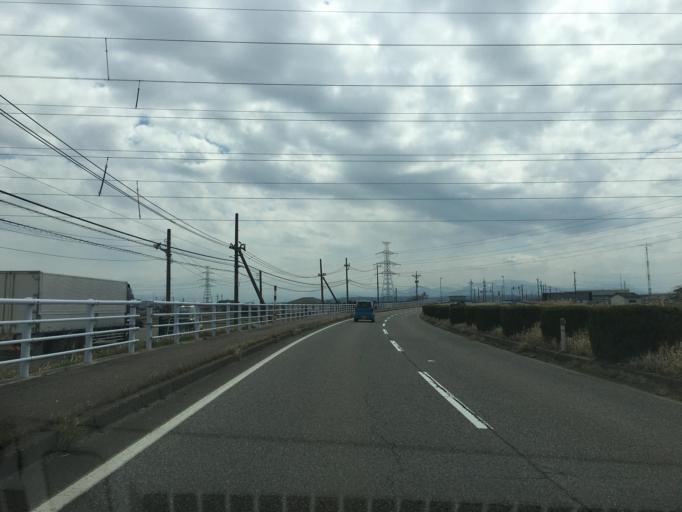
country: JP
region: Toyama
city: Kuragaki-kosugi
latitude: 36.7391
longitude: 137.1301
